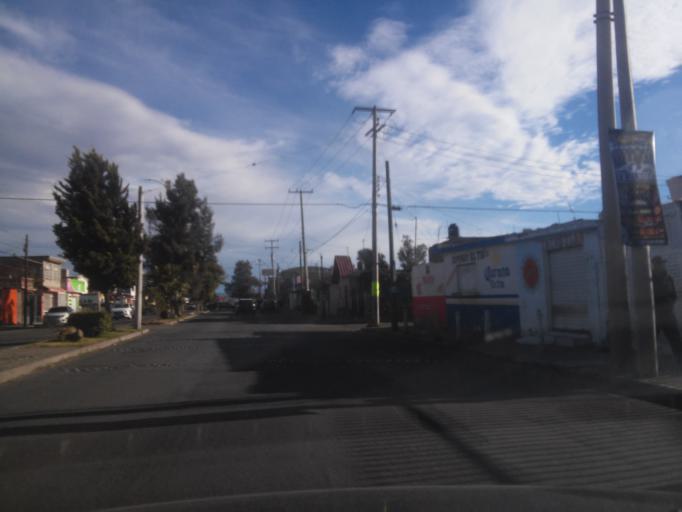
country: MX
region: Durango
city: Victoria de Durango
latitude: 24.0037
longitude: -104.6442
